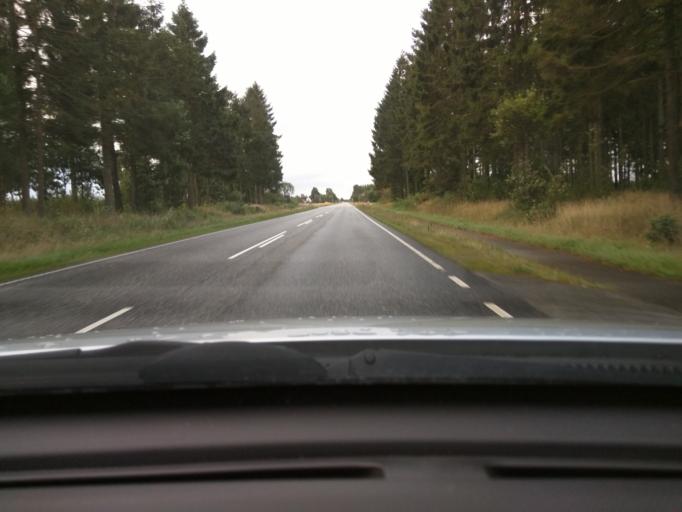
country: DK
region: Central Jutland
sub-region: Ikast-Brande Kommune
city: Bording Kirkeby
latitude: 56.2503
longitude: 9.3209
